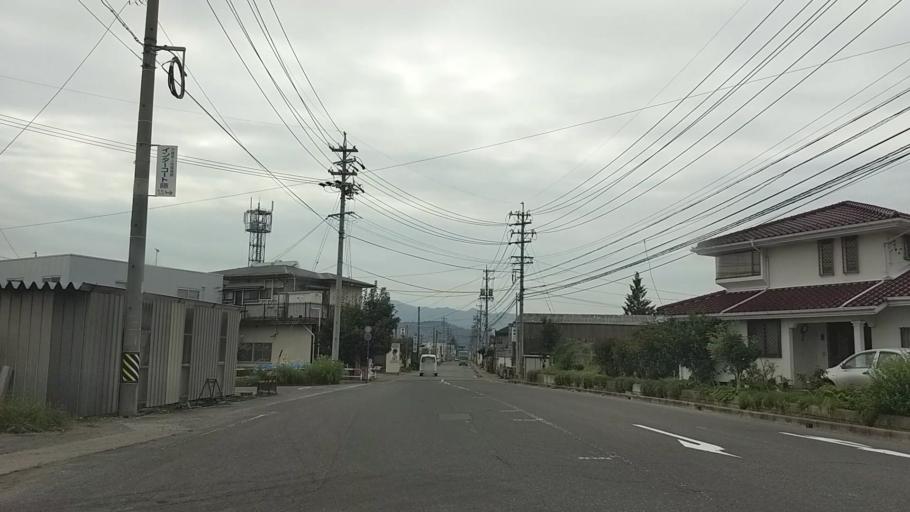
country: JP
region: Nagano
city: Nagano-shi
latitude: 36.6121
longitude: 138.2092
